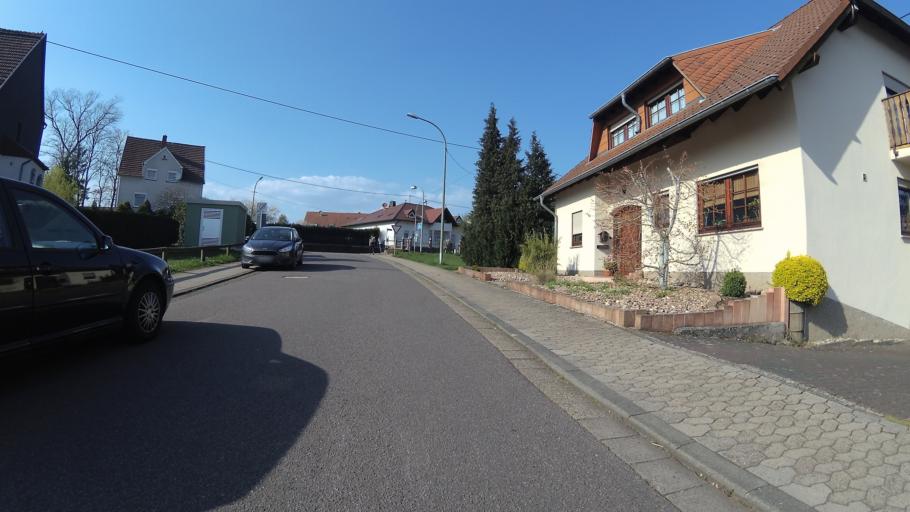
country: DE
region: Saarland
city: Heusweiler
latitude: 49.3362
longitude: 6.9357
